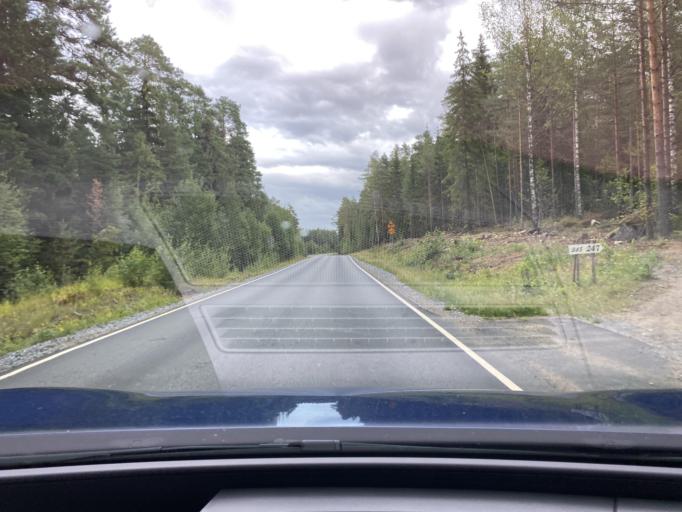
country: FI
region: Pirkanmaa
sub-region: Lounais-Pirkanmaa
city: Vammala
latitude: 61.3001
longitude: 22.9707
